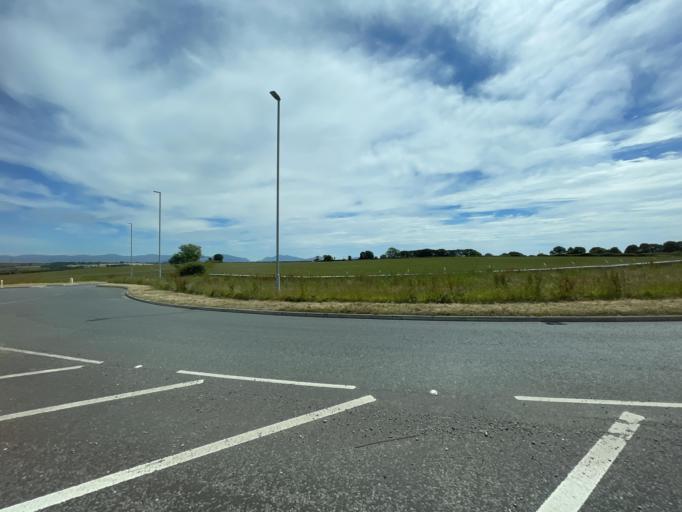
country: GB
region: Wales
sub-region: Anglesey
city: Llangefni
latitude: 53.2457
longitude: -4.3173
